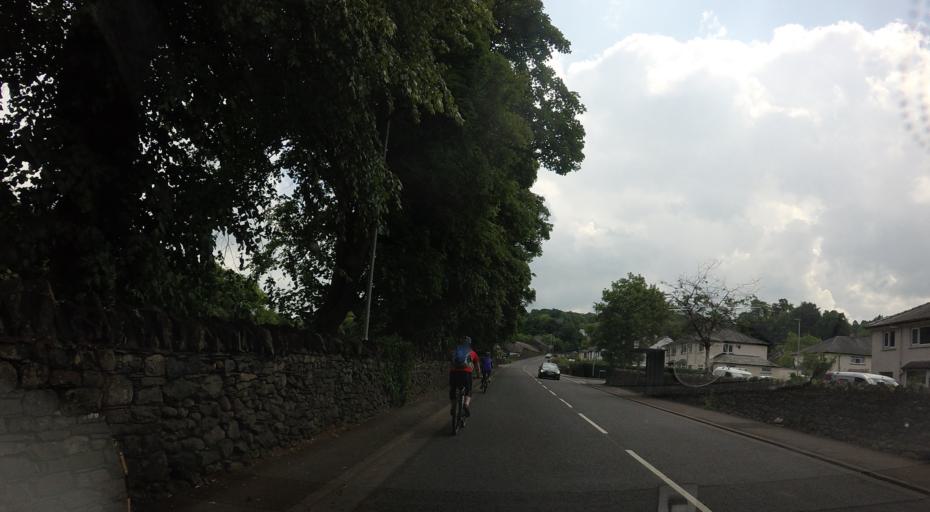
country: GB
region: England
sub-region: Cumbria
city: Keswick
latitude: 54.6048
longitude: -3.1214
